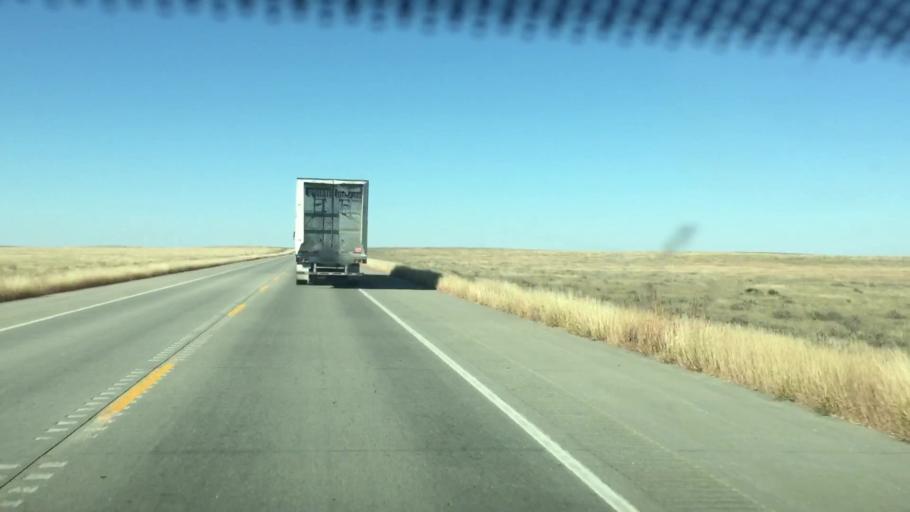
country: US
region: Colorado
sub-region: Kiowa County
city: Eads
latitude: 38.5170
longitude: -102.7857
